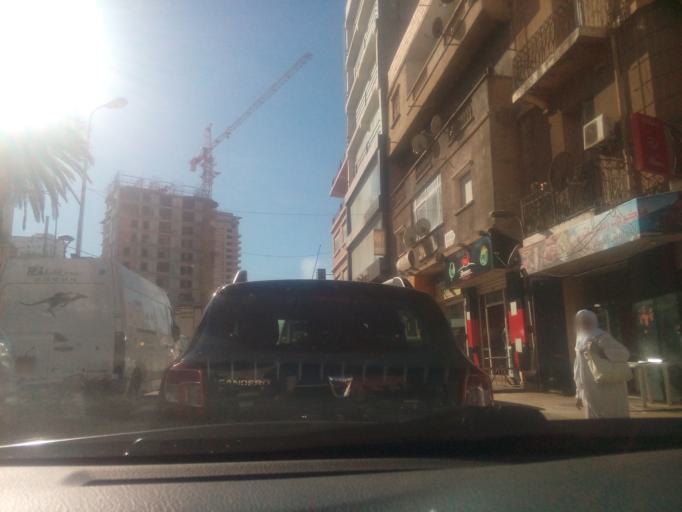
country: DZ
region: Oran
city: Oran
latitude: 35.7079
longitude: -0.6213
